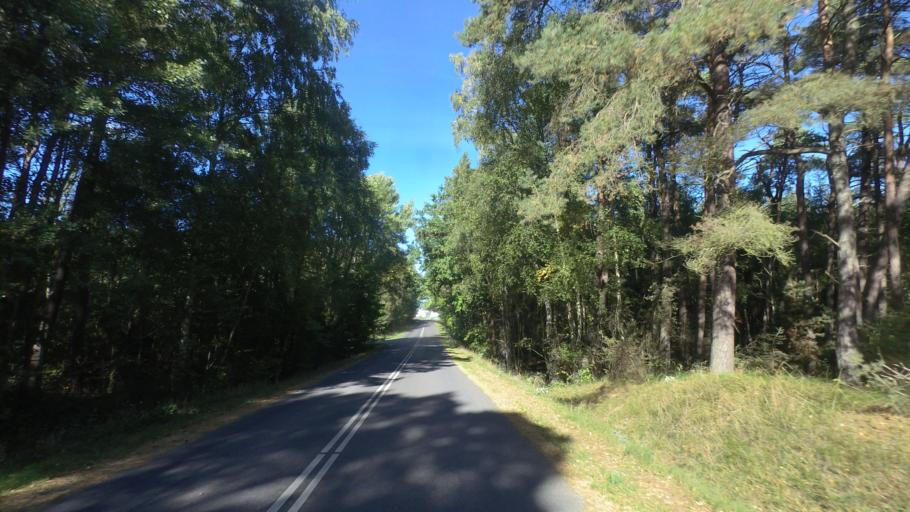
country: DK
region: Capital Region
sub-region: Bornholm Kommune
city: Nexo
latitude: 55.0001
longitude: 15.0754
